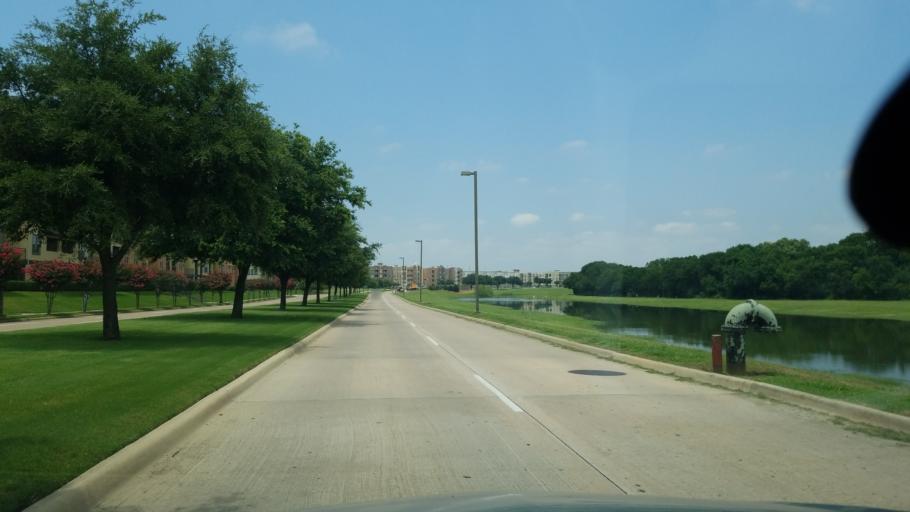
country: US
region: Texas
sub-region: Dallas County
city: Irving
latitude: 32.8678
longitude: -96.9300
